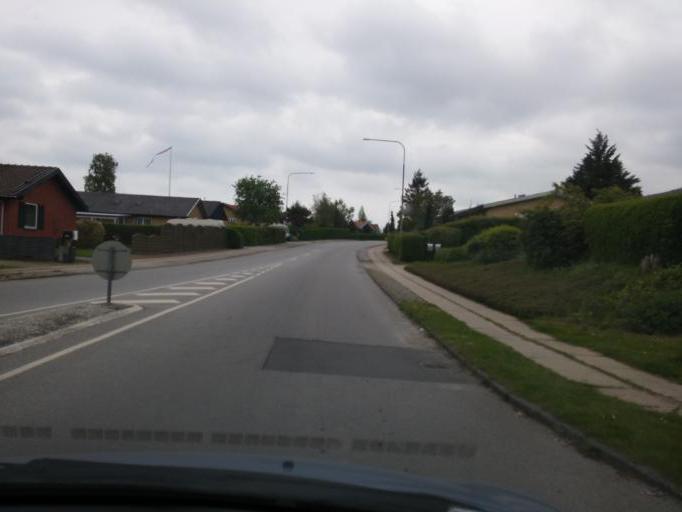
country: DK
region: South Denmark
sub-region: Kerteminde Kommune
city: Kerteminde
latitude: 55.4554
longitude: 10.6509
